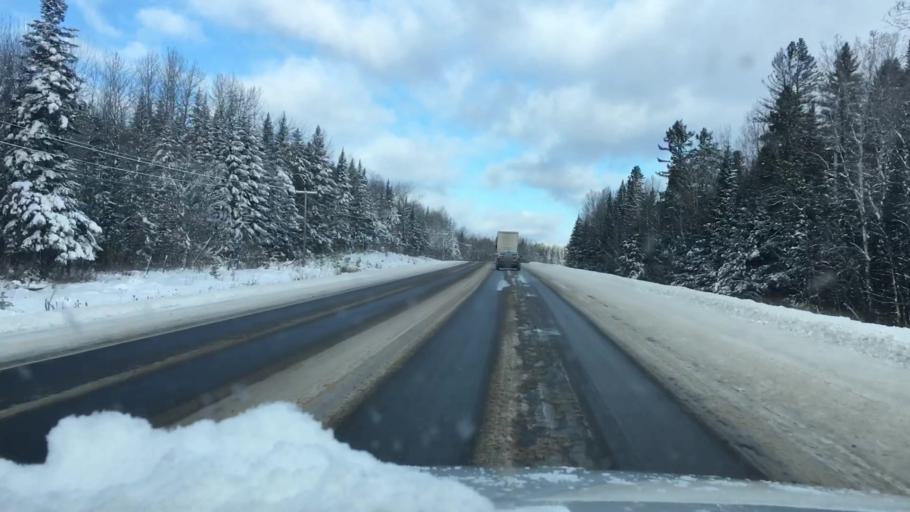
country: US
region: Maine
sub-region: Aroostook County
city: Caribou
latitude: 46.8354
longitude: -67.9983
